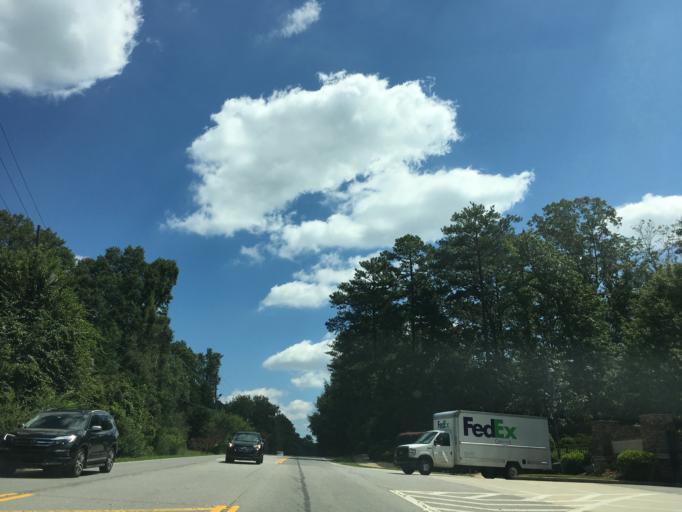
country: US
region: Georgia
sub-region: Fulton County
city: Milton
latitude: 34.1182
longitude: -84.2814
